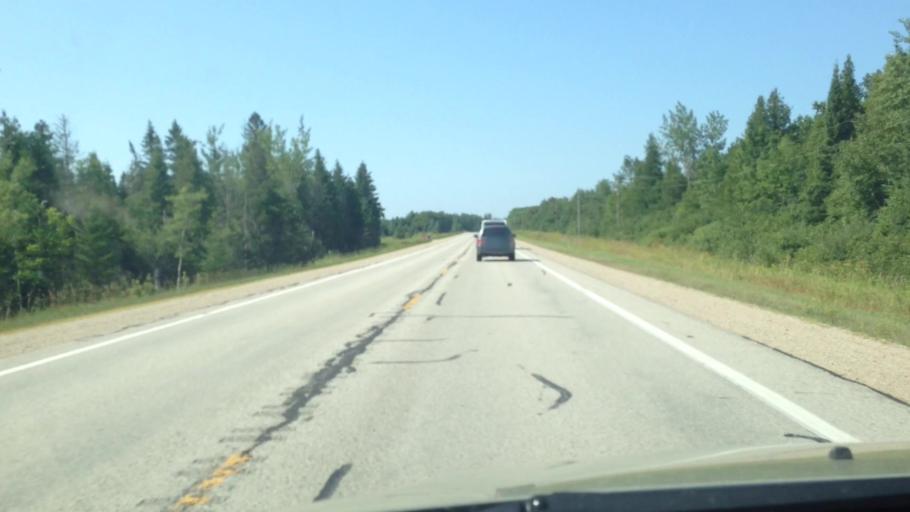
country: US
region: Michigan
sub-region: Delta County
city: Escanaba
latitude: 45.5665
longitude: -87.2567
